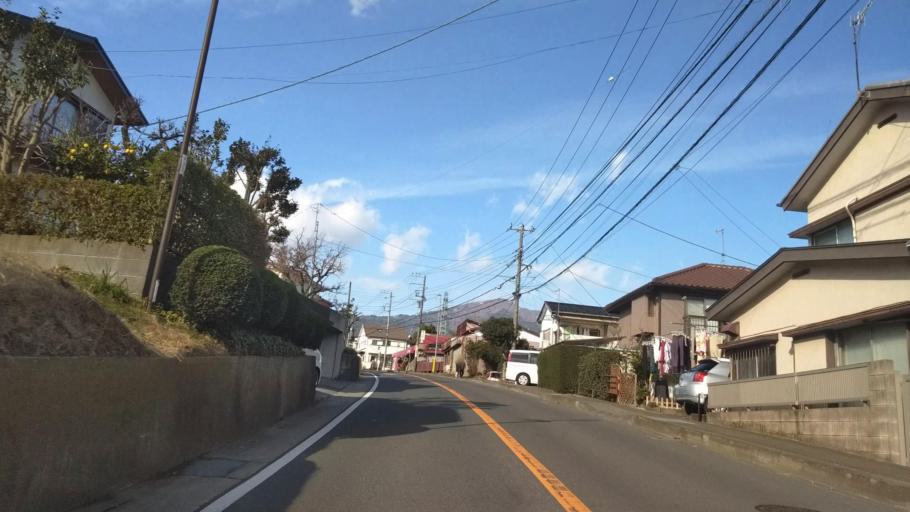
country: JP
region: Kanagawa
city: Hadano
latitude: 35.3845
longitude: 139.2377
